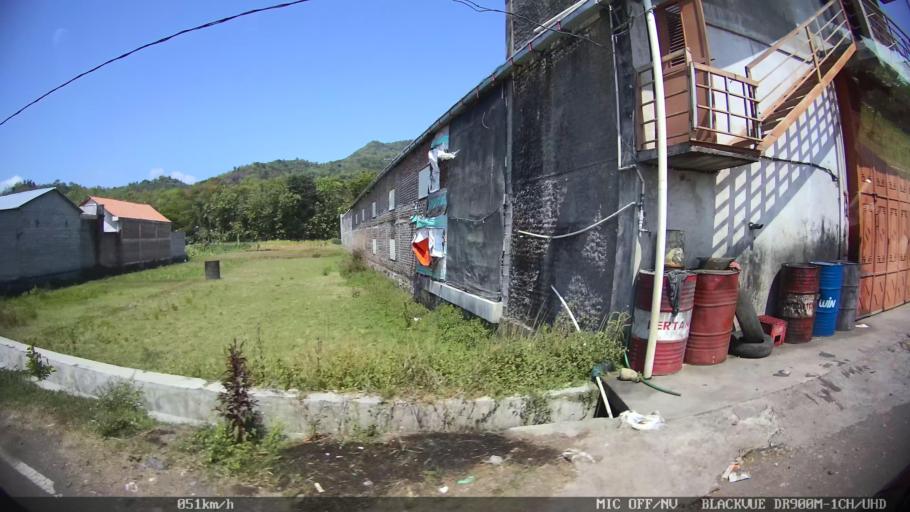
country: ID
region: Daerah Istimewa Yogyakarta
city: Pundong
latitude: -7.9661
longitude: 110.3545
